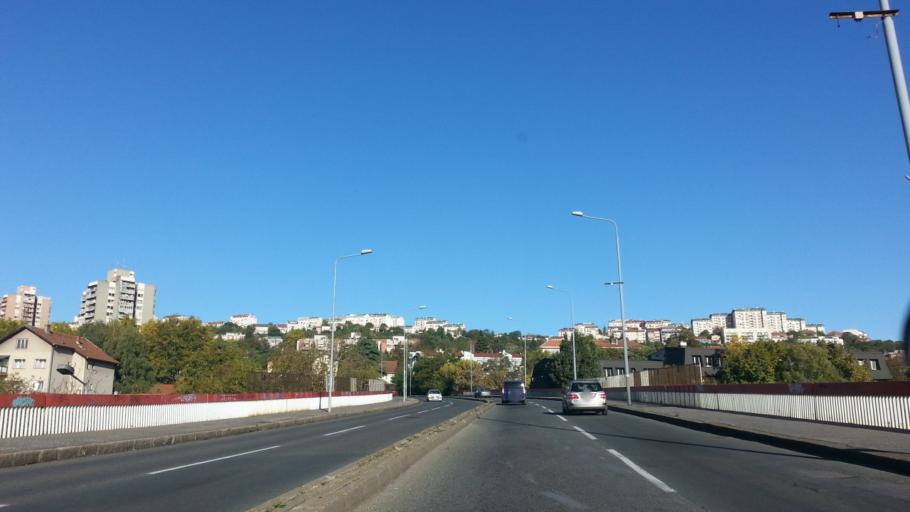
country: RS
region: Central Serbia
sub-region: Belgrade
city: Rakovica
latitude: 44.7444
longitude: 20.4420
